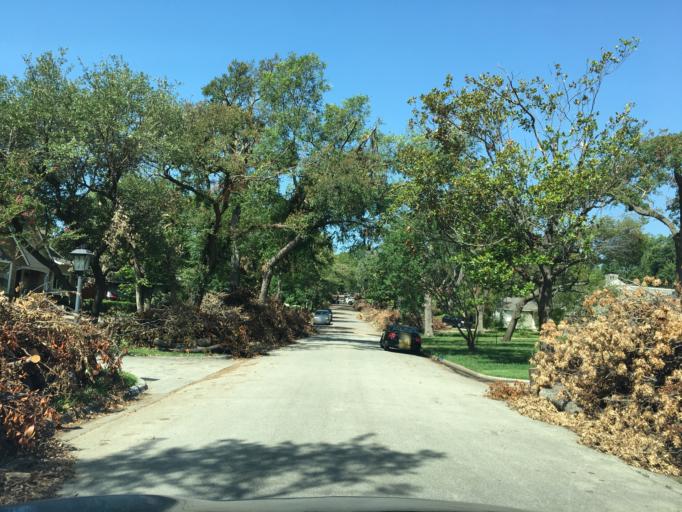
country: US
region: Texas
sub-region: Dallas County
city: Richardson
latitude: 32.9076
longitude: -96.7752
